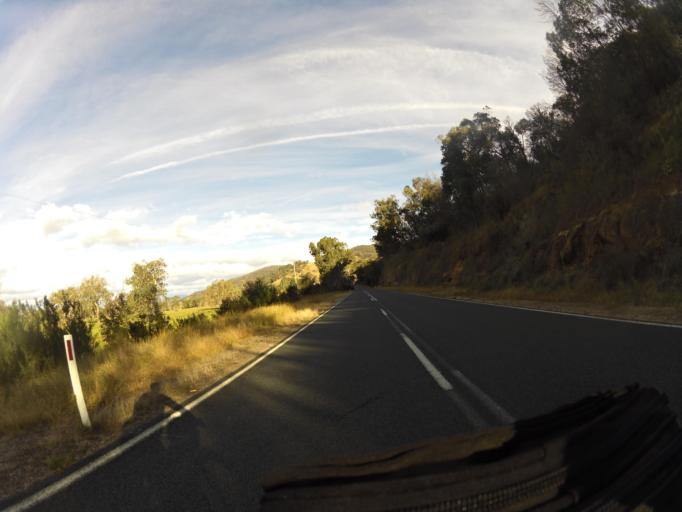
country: AU
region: New South Wales
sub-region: Greater Hume Shire
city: Holbrook
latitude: -35.9967
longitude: 147.8666
